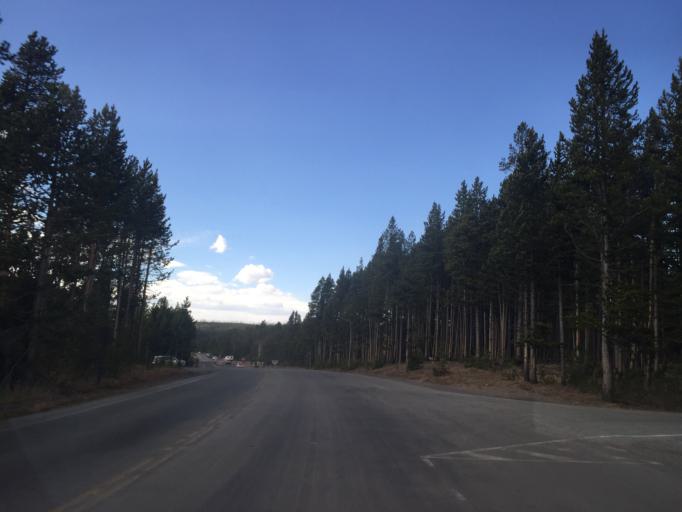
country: US
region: Montana
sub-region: Gallatin County
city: West Yellowstone
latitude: 44.7357
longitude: -110.4902
